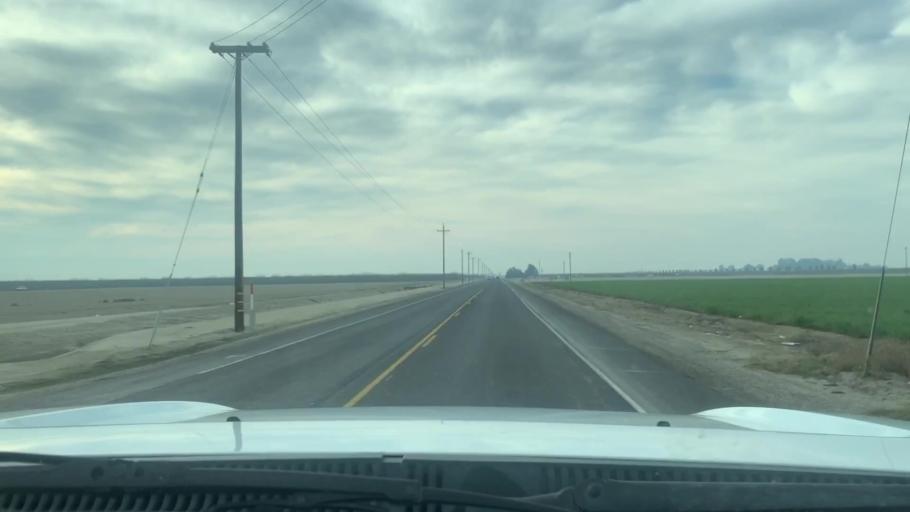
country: US
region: California
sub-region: Kern County
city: Buttonwillow
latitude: 35.4422
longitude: -119.4117
